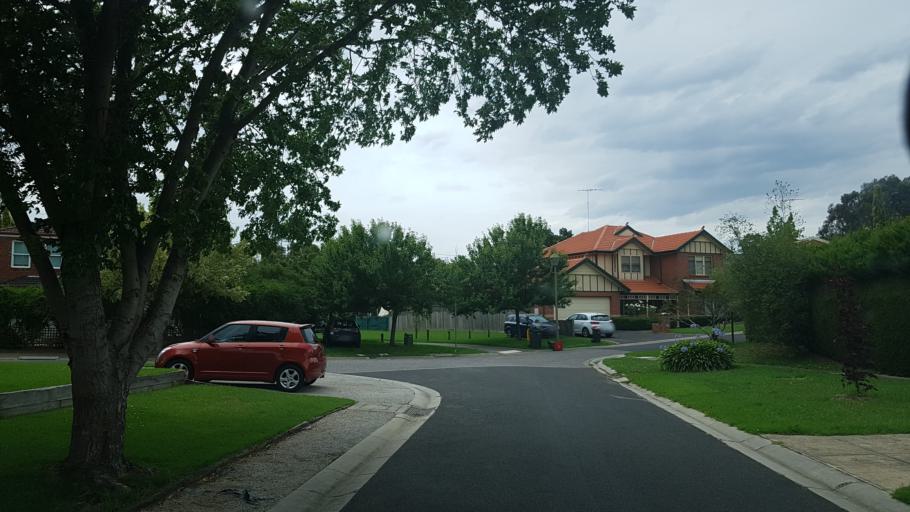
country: AU
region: Victoria
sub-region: Manningham
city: Bulleen
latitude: -37.7569
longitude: 145.0925
